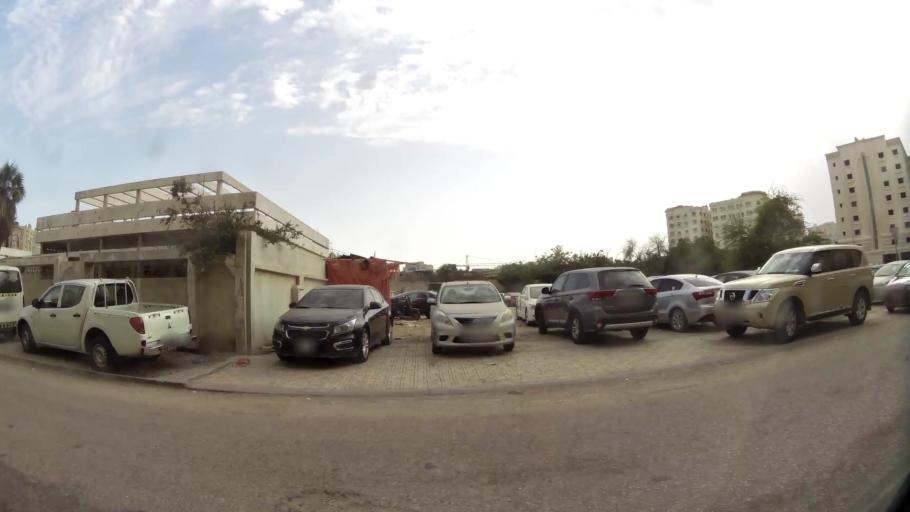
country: QA
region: Baladiyat ad Dawhah
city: Doha
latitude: 25.2834
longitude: 51.5164
